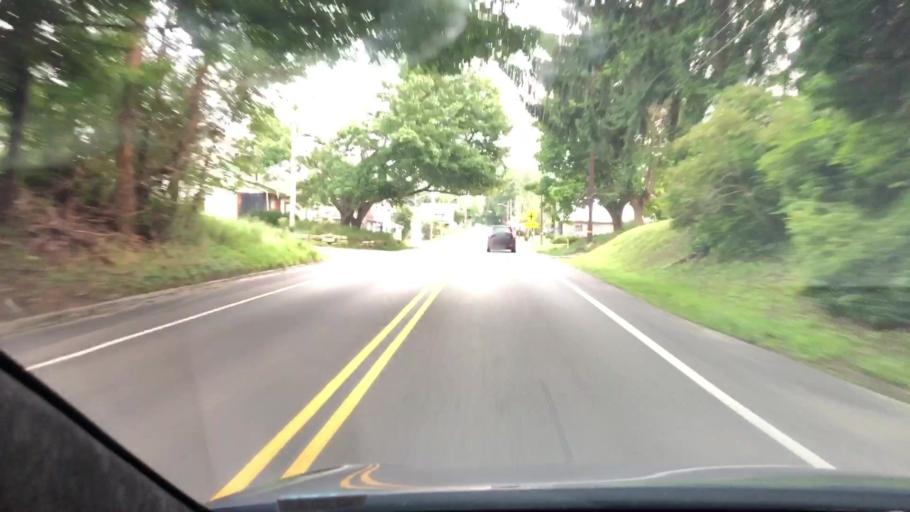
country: US
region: Pennsylvania
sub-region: Butler County
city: Slippery Rock
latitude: 41.1083
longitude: -80.0062
